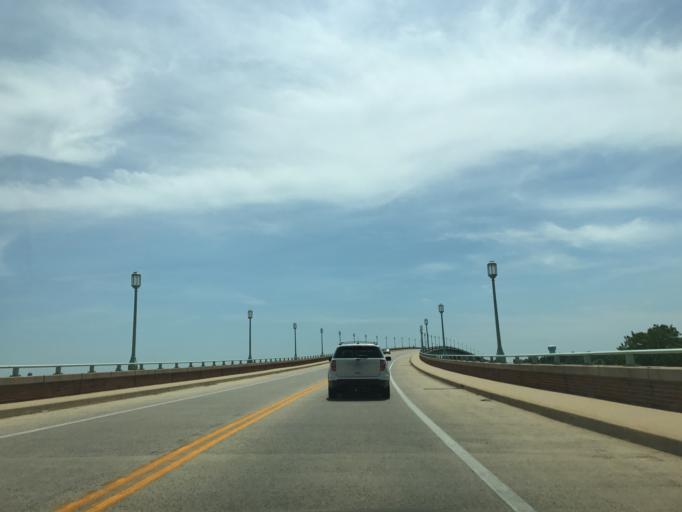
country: US
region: Maryland
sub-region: Anne Arundel County
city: Naval Academy
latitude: 38.9957
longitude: -76.4836
